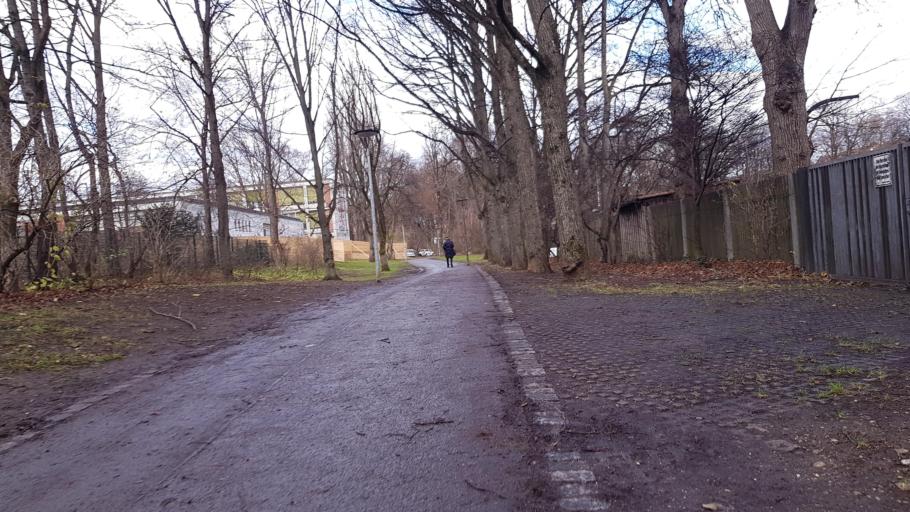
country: DE
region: Bavaria
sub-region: Upper Bavaria
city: Munich
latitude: 48.1146
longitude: 11.5454
